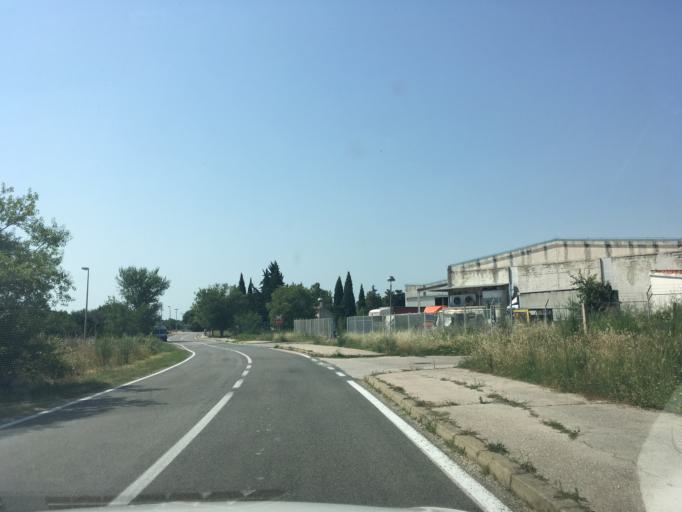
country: HR
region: Zadarska
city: Benkovac
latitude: 44.0246
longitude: 15.6179
